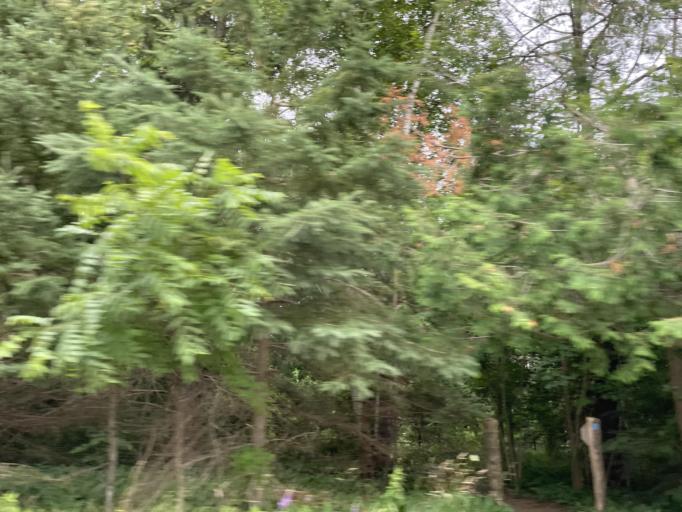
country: CA
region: Ontario
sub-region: Wellington County
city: Guelph
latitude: 43.5987
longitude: -80.2665
